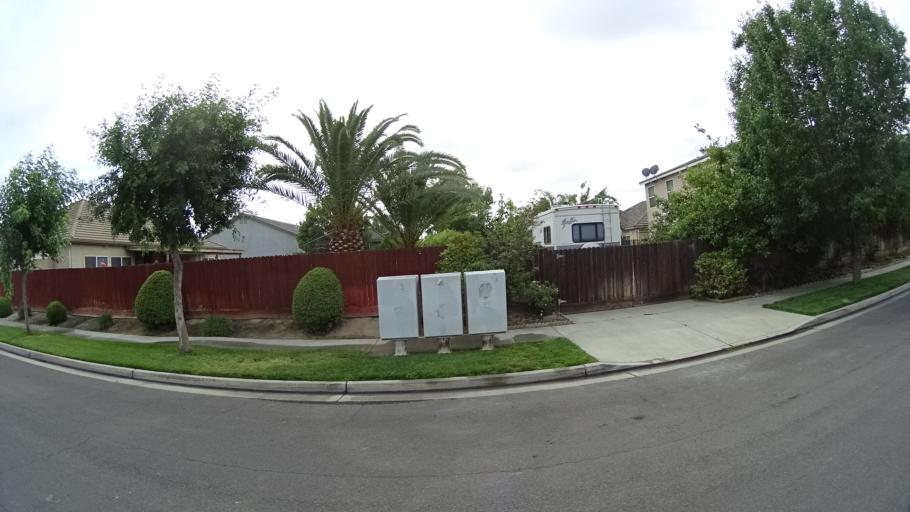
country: US
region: California
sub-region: Kings County
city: Hanford
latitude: 36.3338
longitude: -119.6770
